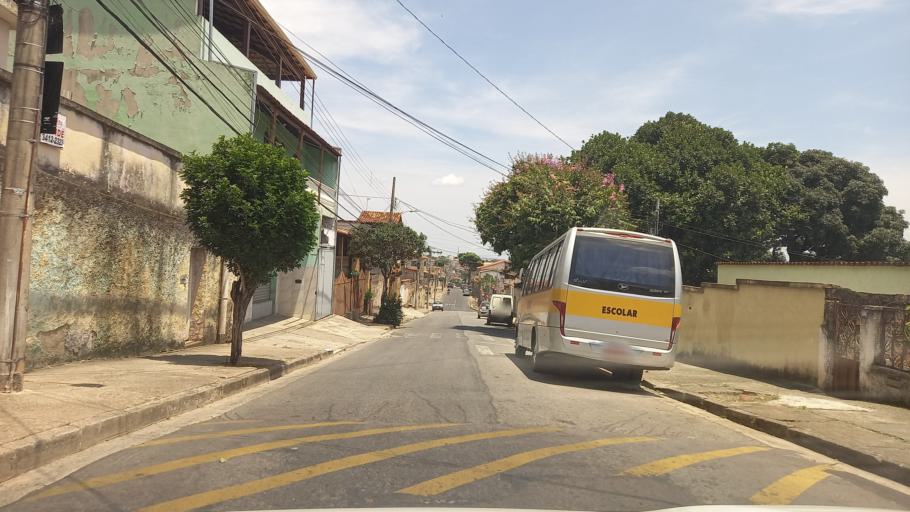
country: BR
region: Minas Gerais
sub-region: Contagem
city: Contagem
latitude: -19.9069
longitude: -44.0093
